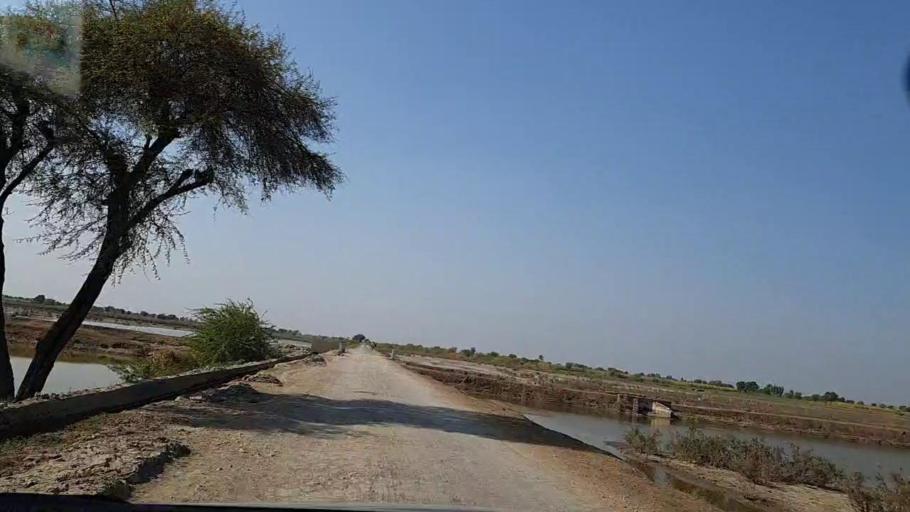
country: PK
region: Sindh
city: Digri
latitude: 25.1683
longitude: 69.0653
